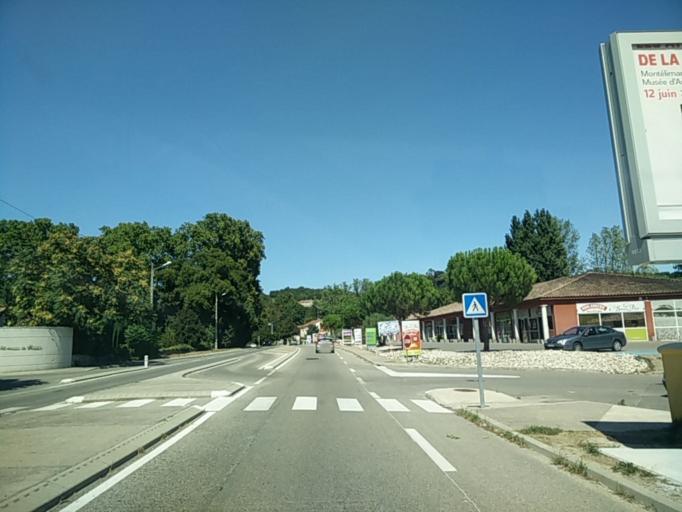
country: FR
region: Rhone-Alpes
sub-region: Departement de la Drome
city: Montelimar
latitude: 44.5482
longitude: 4.7738
